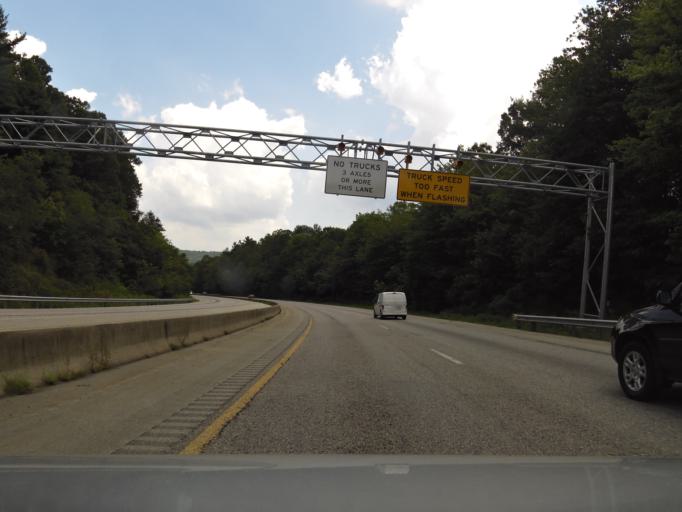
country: US
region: North Carolina
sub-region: Henderson County
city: East Flat Rock
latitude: 35.2754
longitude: -82.3866
